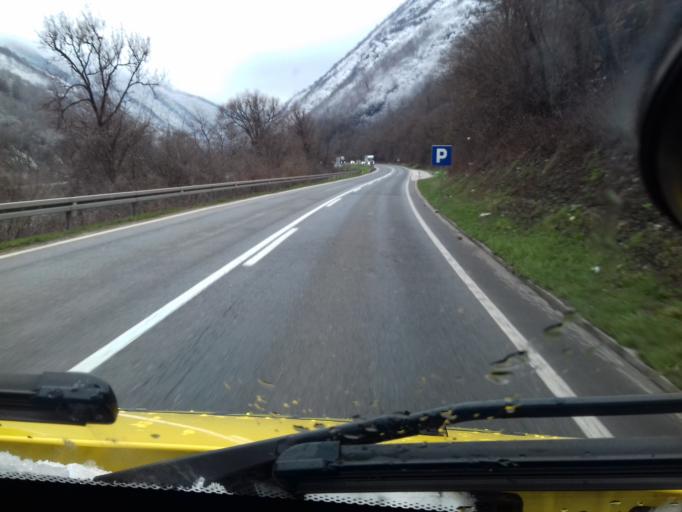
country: BA
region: Federation of Bosnia and Herzegovina
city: Lokvine
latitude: 44.2632
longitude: 17.8813
